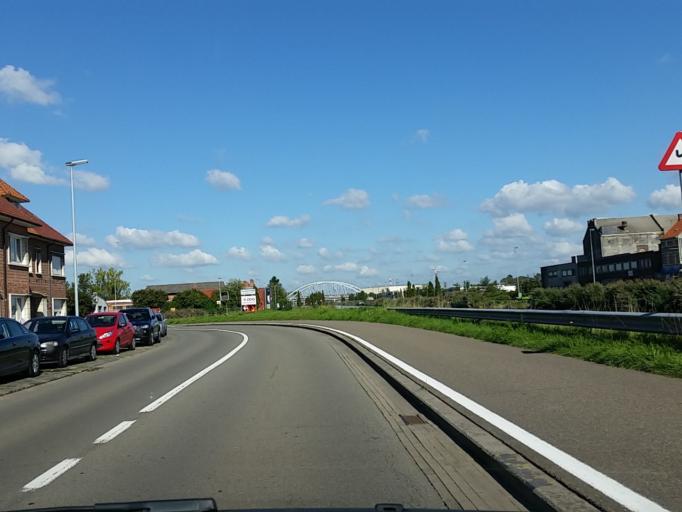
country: BE
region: Flanders
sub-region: Provincie Vlaams-Brabant
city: Leuven
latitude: 50.8929
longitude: 4.7062
